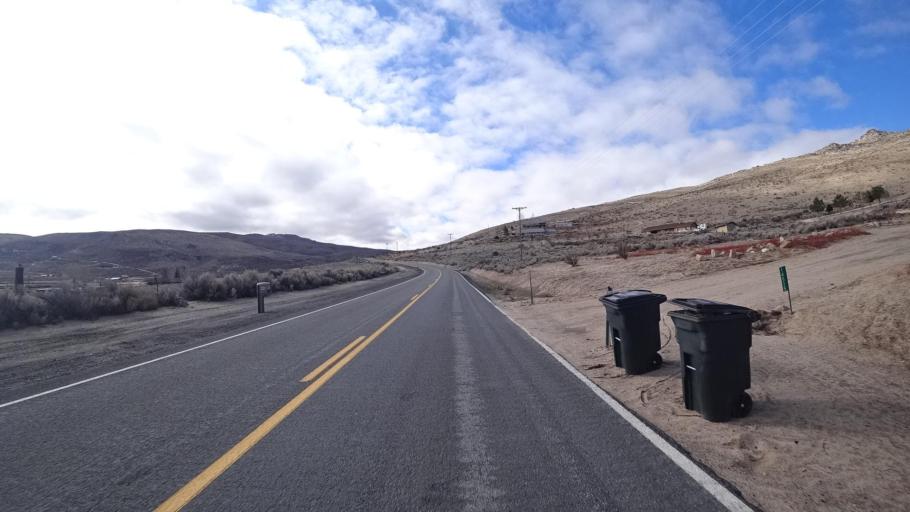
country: US
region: Nevada
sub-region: Washoe County
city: Cold Springs
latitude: 39.8473
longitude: -119.9354
